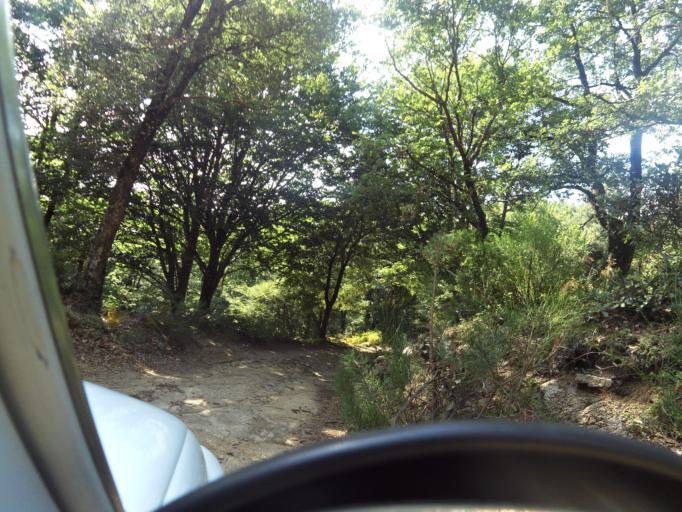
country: IT
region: Calabria
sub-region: Provincia di Vibo-Valentia
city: Nardodipace
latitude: 38.5104
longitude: 16.3875
